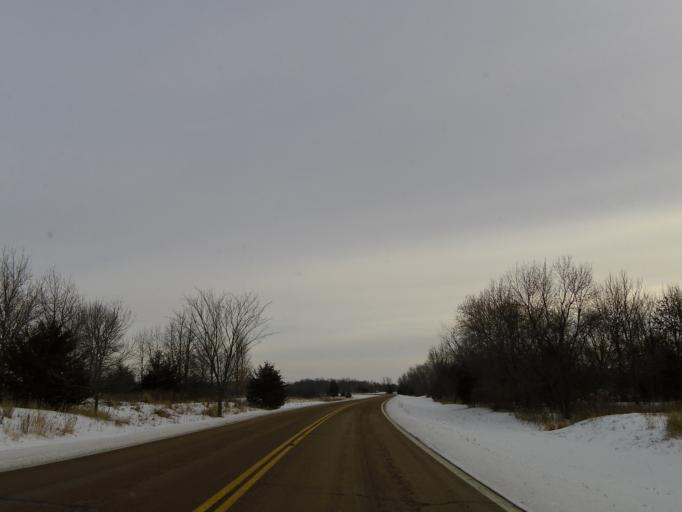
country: US
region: Minnesota
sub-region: Carver County
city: Victoria
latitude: 44.8769
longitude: -93.6933
